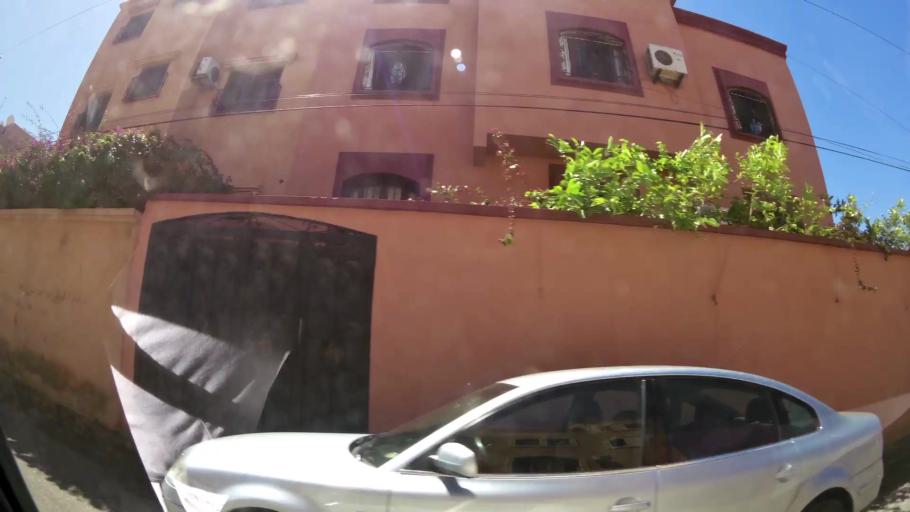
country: MA
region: Marrakech-Tensift-Al Haouz
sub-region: Marrakech
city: Marrakesh
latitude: 31.6547
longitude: -7.9869
